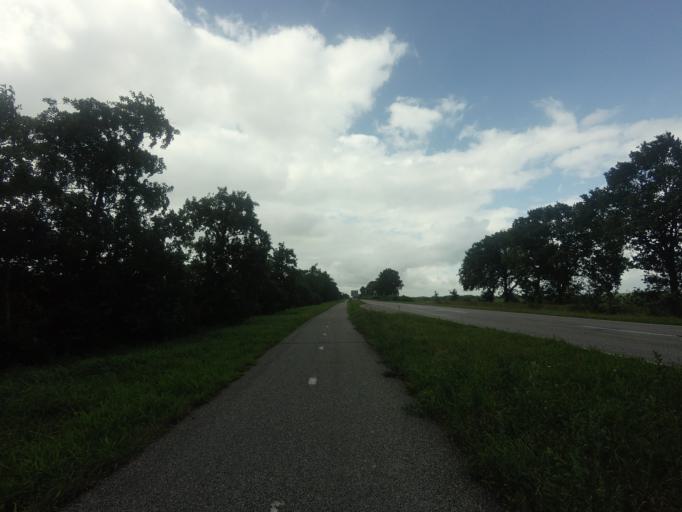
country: NL
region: Friesland
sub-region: Gemeente Skarsterlan
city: Joure
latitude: 52.9665
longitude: 5.7717
